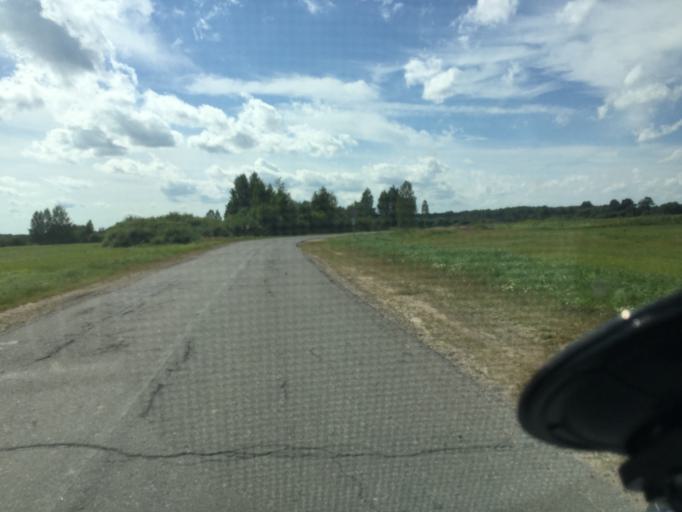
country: BY
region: Vitebsk
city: Chashniki
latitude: 55.3121
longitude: 29.4171
